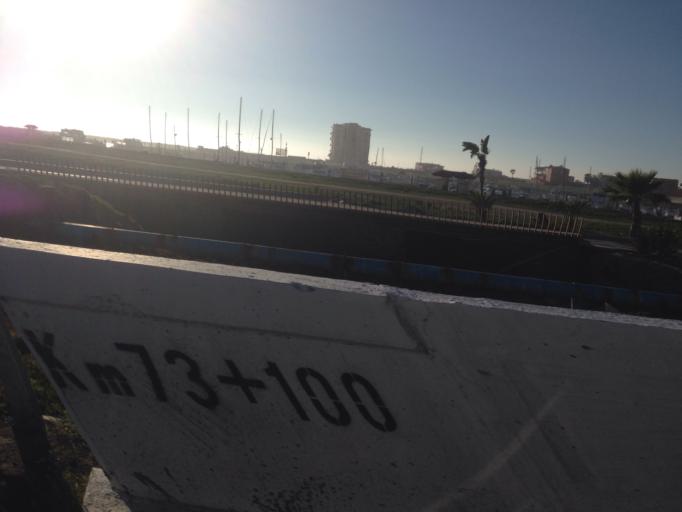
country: MX
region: Baja California
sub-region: Playas de Rosarito
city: Santa Anita
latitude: 32.0562
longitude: -116.8773
